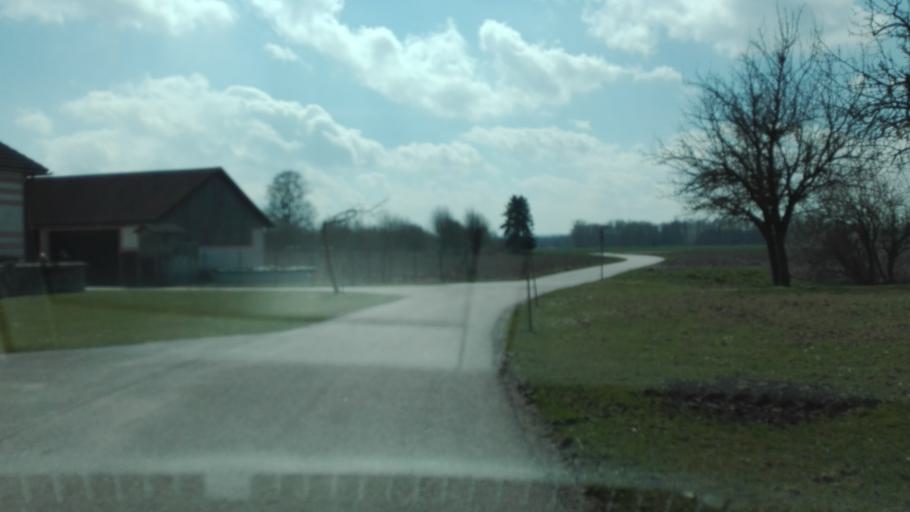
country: AT
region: Upper Austria
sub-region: Politischer Bezirk Urfahr-Umgebung
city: Feldkirchen an der Donau
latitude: 48.3409
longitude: 14.0460
